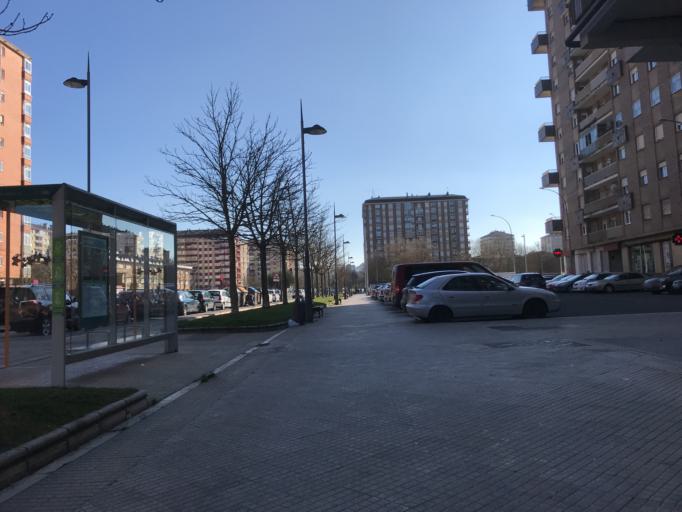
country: ES
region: Basque Country
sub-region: Provincia de Alava
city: Gasteiz / Vitoria
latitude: 42.8454
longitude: -2.6585
